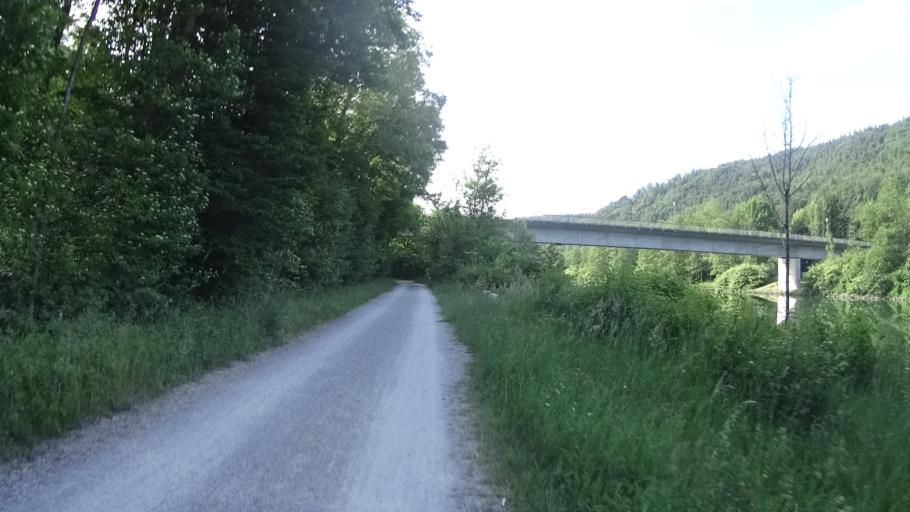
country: DE
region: Bavaria
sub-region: Lower Bavaria
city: Essing
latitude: 48.9468
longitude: 11.7418
